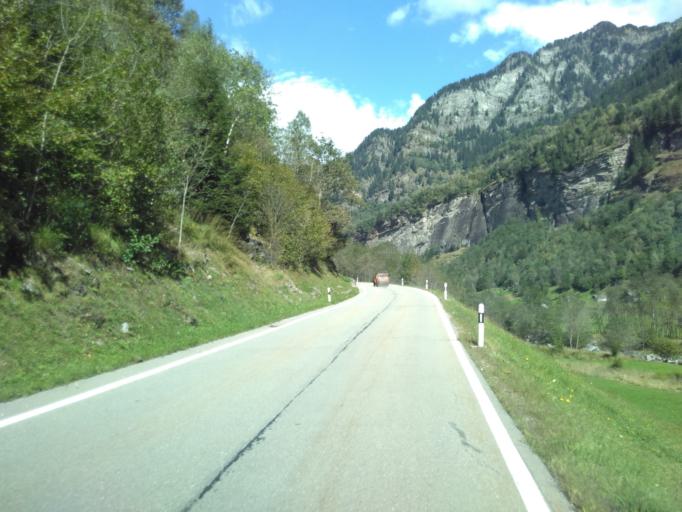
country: CH
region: Grisons
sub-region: Moesa District
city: Cauco
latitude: 46.3231
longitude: 9.1177
